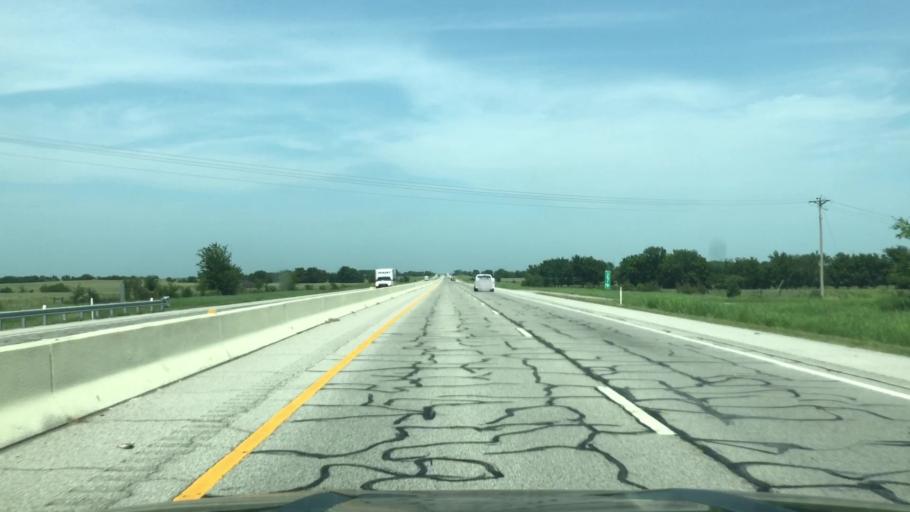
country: US
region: Oklahoma
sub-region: Craig County
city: Vinita
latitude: 36.5245
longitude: -95.2545
